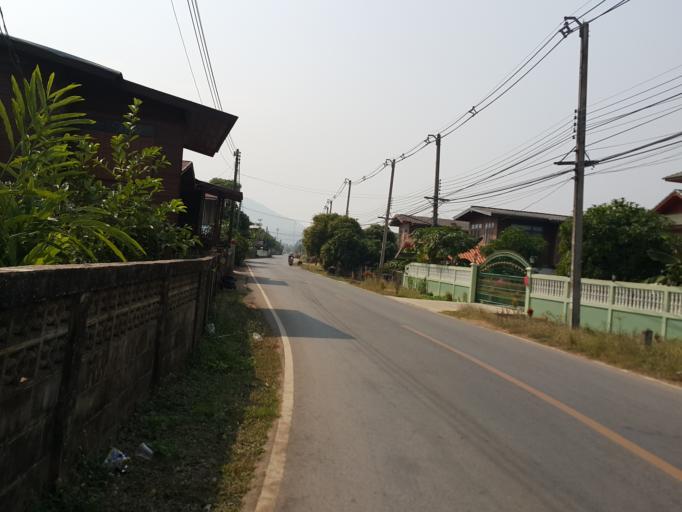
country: TH
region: Sukhothai
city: Thung Saliam
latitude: 17.3282
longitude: 99.5308
